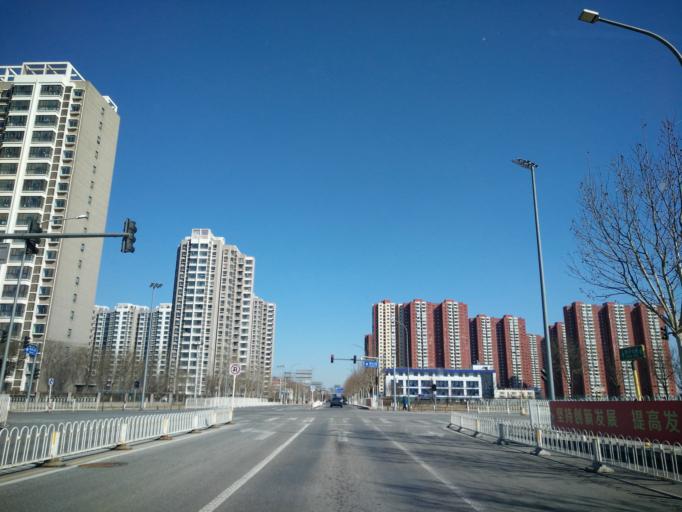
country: CN
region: Beijing
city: Yinghai
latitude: 39.7529
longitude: 116.4941
